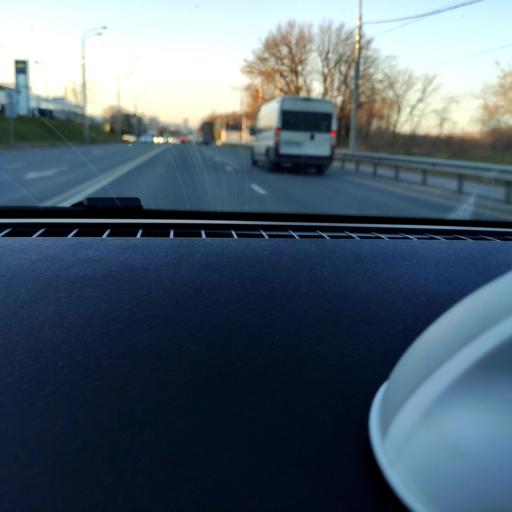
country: RU
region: Samara
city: Samara
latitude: 53.2759
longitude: 50.2272
